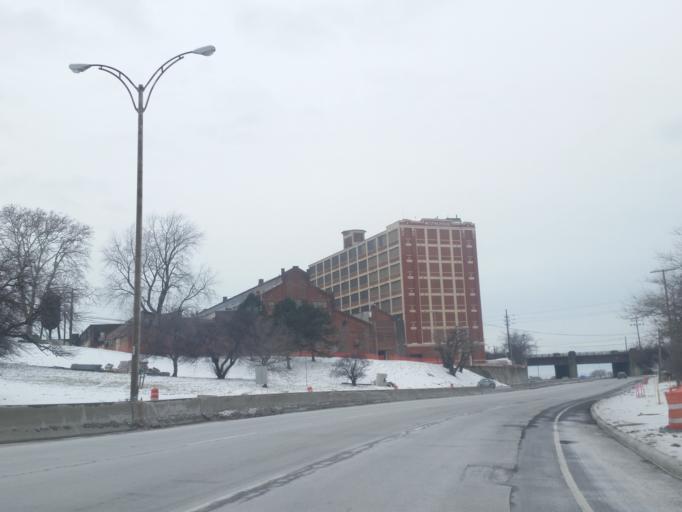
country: US
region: Ohio
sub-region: Cuyahoga County
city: Cleveland
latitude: 41.4898
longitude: -81.7246
